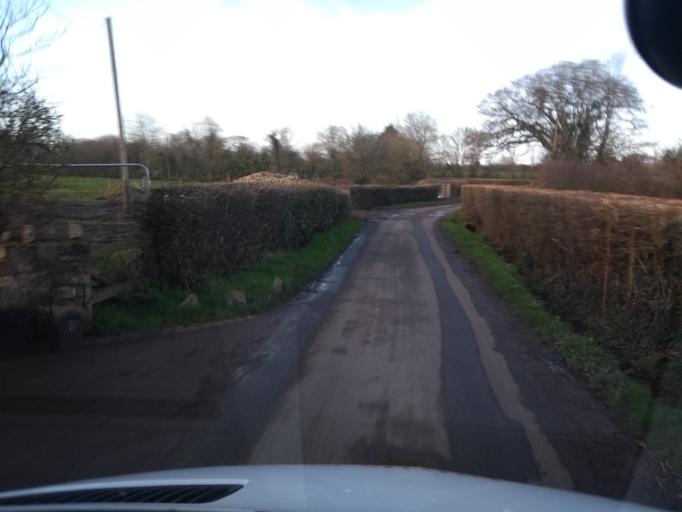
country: GB
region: England
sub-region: Somerset
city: Wedmore
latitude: 51.2383
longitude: -2.8245
